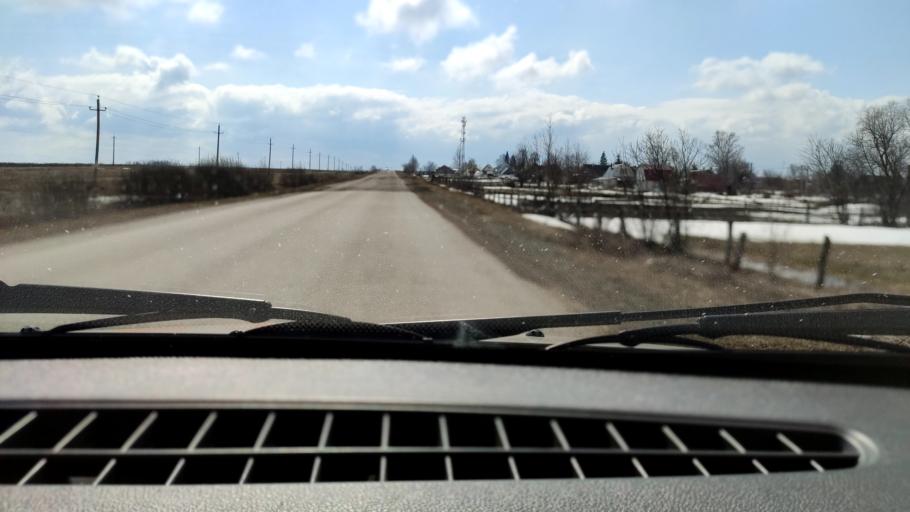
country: RU
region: Bashkortostan
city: Kudeyevskiy
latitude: 54.8503
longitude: 56.7953
